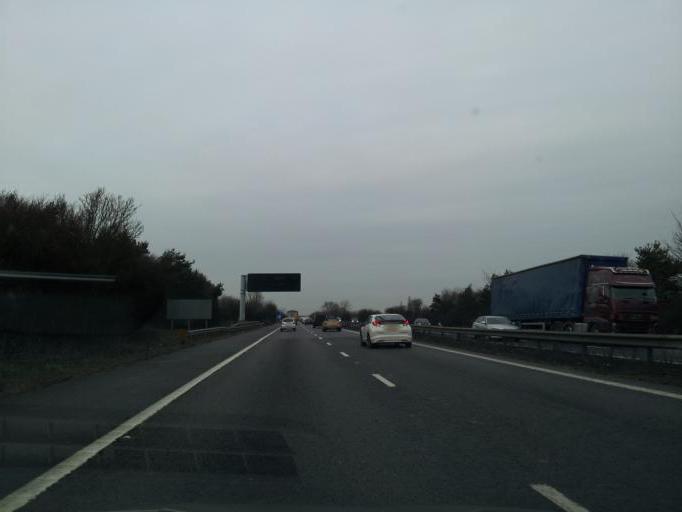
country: GB
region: England
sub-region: Cambridgeshire
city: Barton
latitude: 52.2015
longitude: 0.0753
